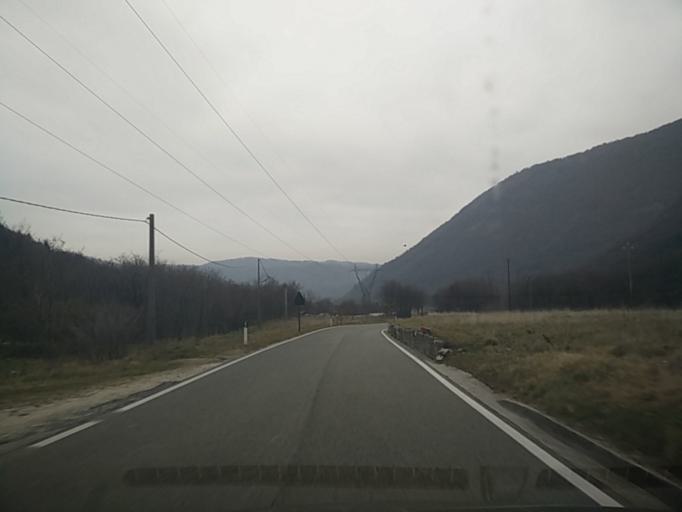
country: IT
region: Veneto
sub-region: Provincia di Treviso
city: Cison di Valmarino
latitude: 45.9886
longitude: 12.1725
